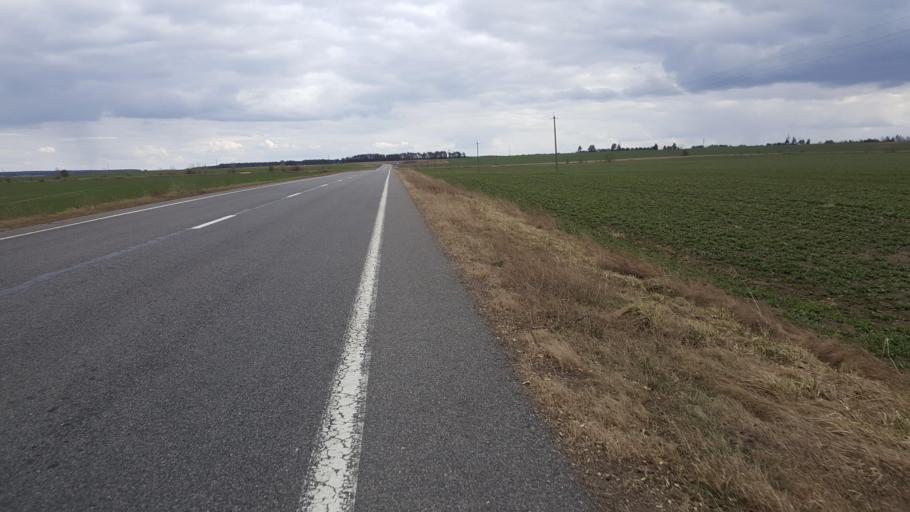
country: BY
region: Brest
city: Kamyanyets
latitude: 52.4147
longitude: 23.8498
